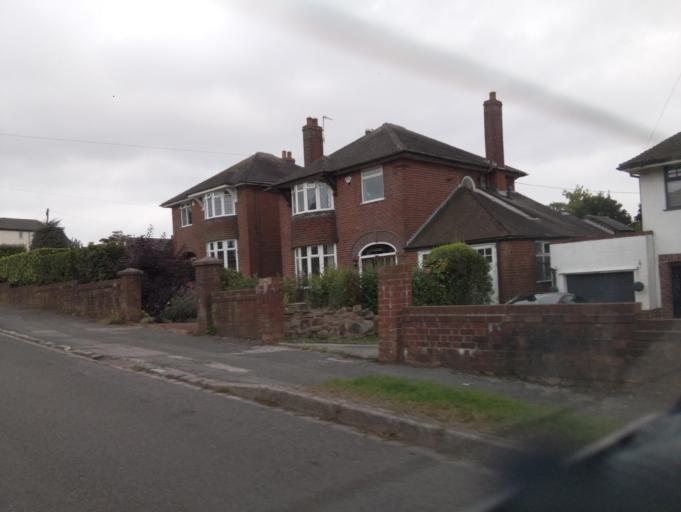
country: GB
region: England
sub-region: Staffordshire
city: Longton
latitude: 53.0214
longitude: -2.1026
